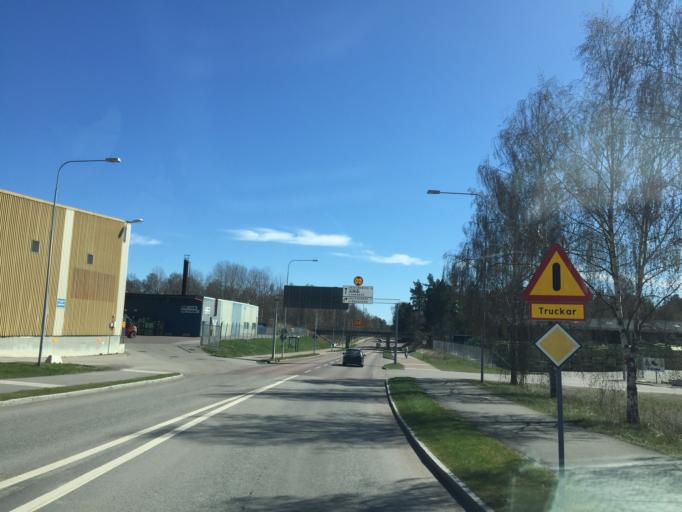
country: SE
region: Kalmar
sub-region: Oskarshamns Kommun
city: Oskarshamn
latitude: 57.2555
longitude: 16.4602
